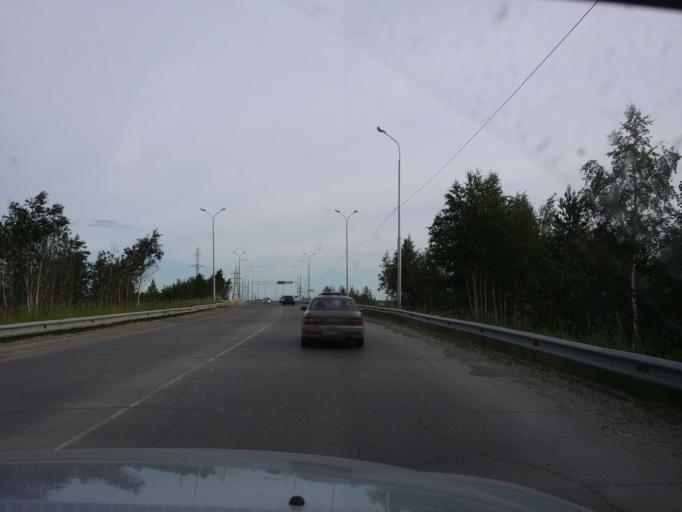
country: RU
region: Khanty-Mansiyskiy Avtonomnyy Okrug
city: Nizhnevartovsk
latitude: 60.9528
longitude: 76.6629
